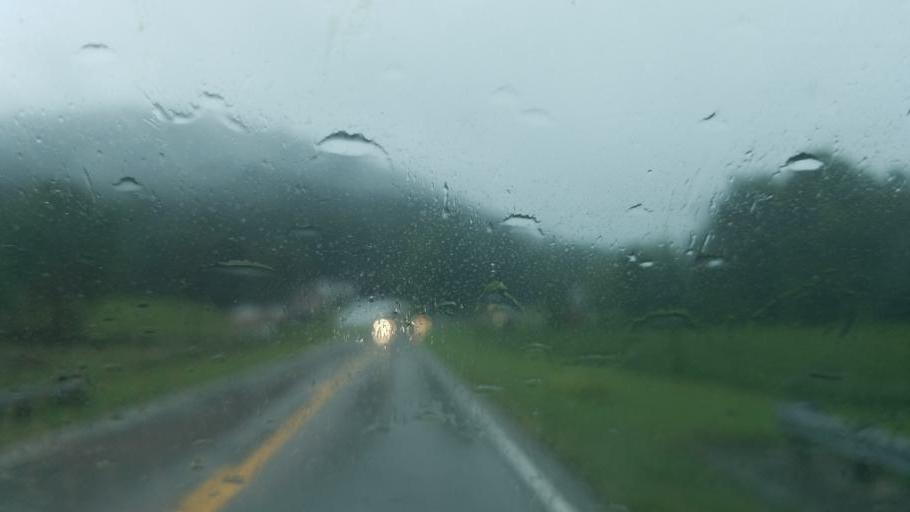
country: US
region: Kentucky
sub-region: Rowan County
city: Morehead
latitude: 38.3084
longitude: -83.5676
